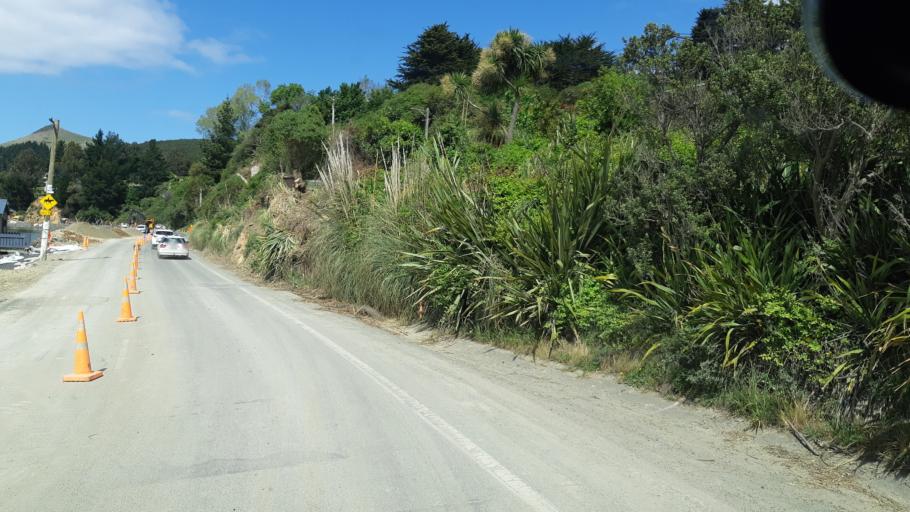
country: NZ
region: Otago
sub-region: Dunedin City
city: Portobello
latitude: -45.8484
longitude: 170.6115
